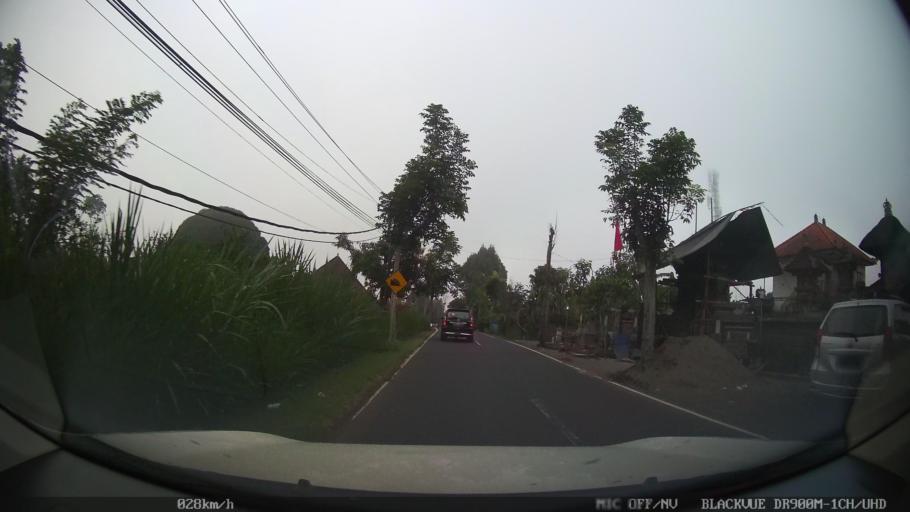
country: ID
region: Bali
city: Banjar Taro Kelod
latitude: -8.3115
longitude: 115.3036
